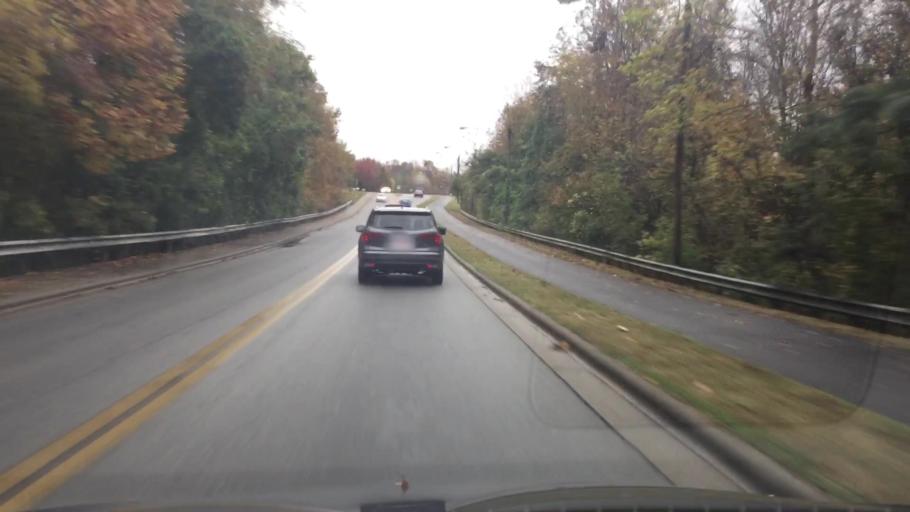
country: US
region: North Carolina
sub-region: Rowan County
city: Salisbury
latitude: 35.6719
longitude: -80.4946
